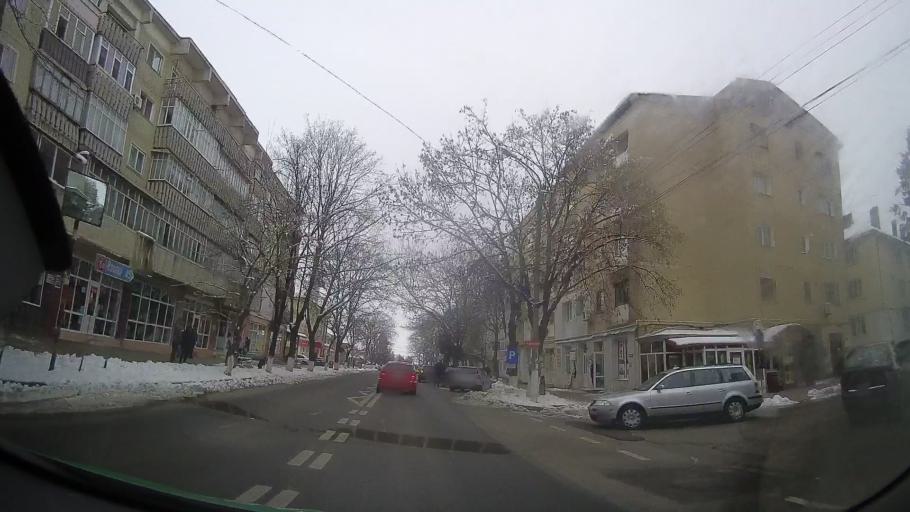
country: RO
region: Vaslui
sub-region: Comuna Negresti
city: Negresti
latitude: 46.8348
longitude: 27.4541
